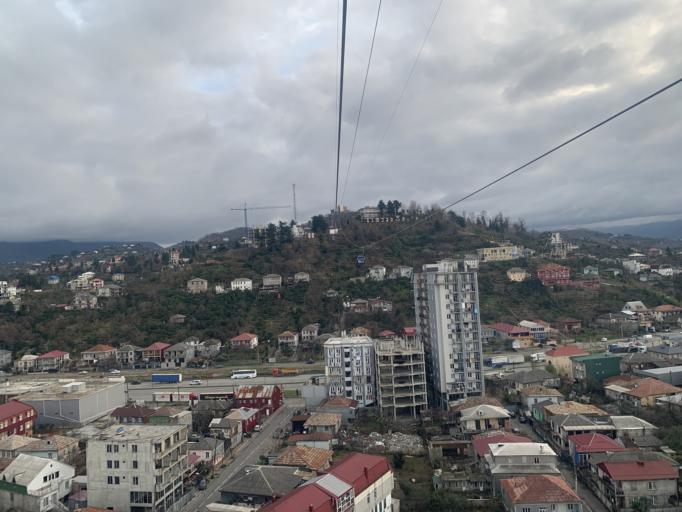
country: GE
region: Ajaria
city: Batumi
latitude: 41.6411
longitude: 41.6486
